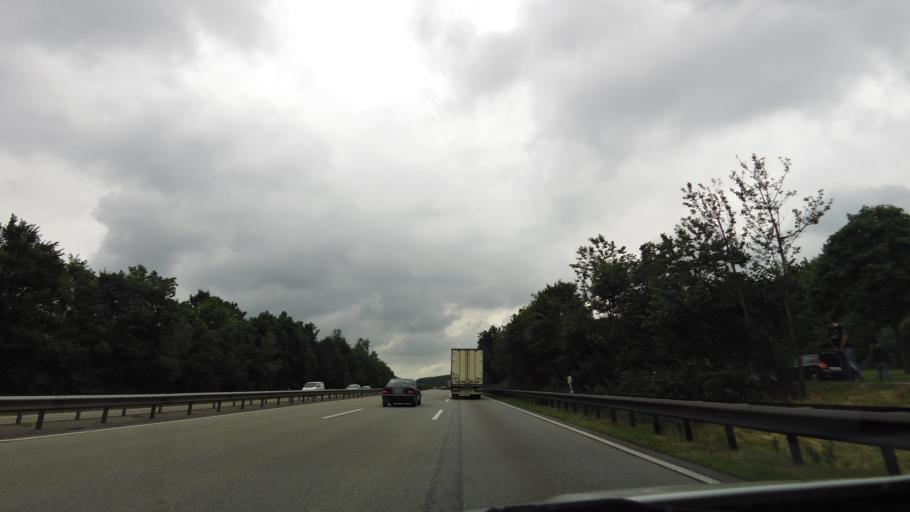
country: DE
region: Rheinland-Pfalz
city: Konigsfeld
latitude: 50.5162
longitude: 7.2011
